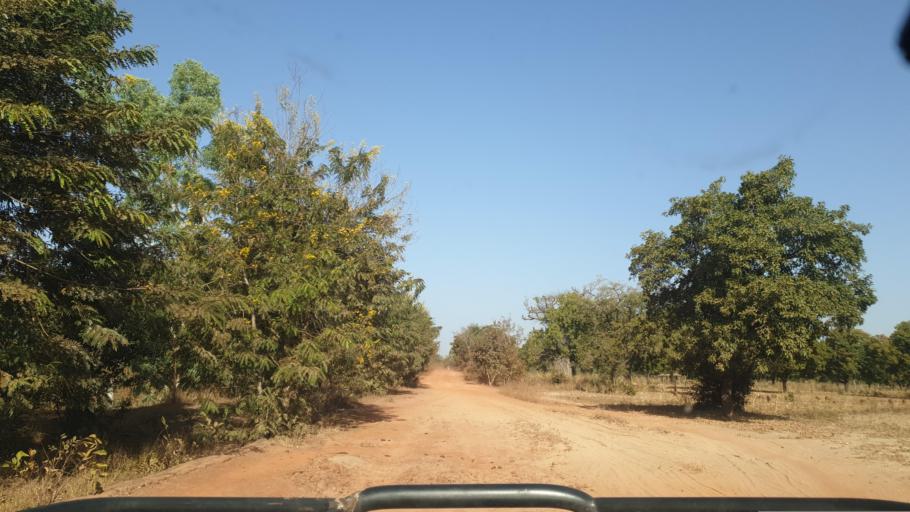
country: ML
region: Sikasso
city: Bougouni
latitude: 11.7740
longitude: -6.9042
